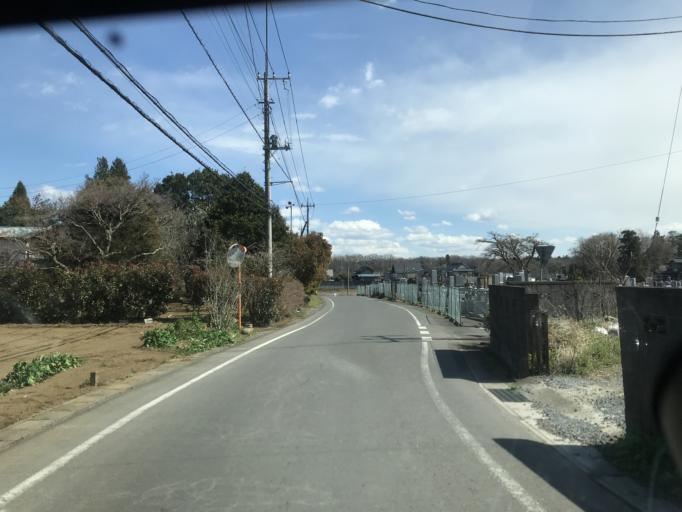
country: JP
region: Ibaraki
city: Shimodate
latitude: 36.2344
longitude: 139.9352
